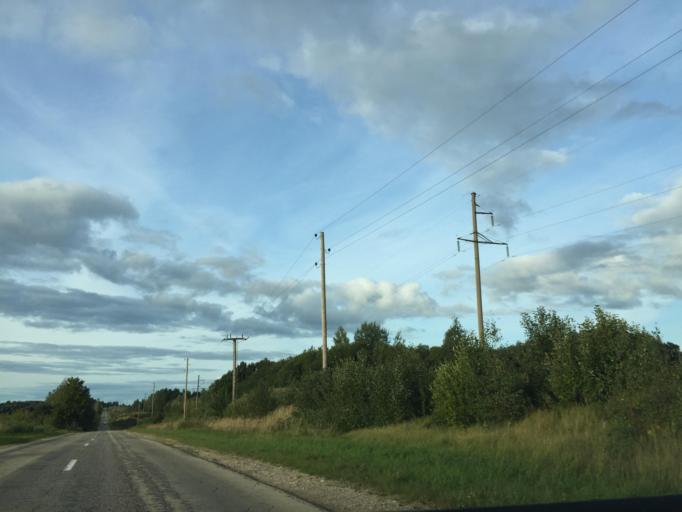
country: LV
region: Nereta
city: Nereta
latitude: 56.2310
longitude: 25.3237
